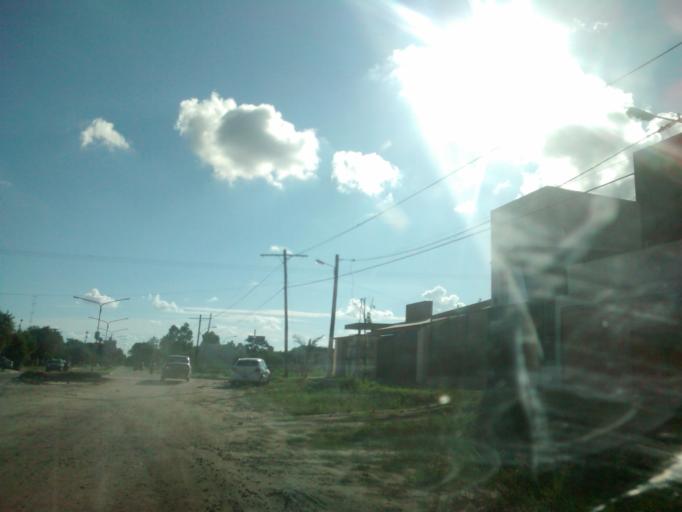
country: AR
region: Chaco
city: Resistencia
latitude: -27.4395
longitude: -58.9649
